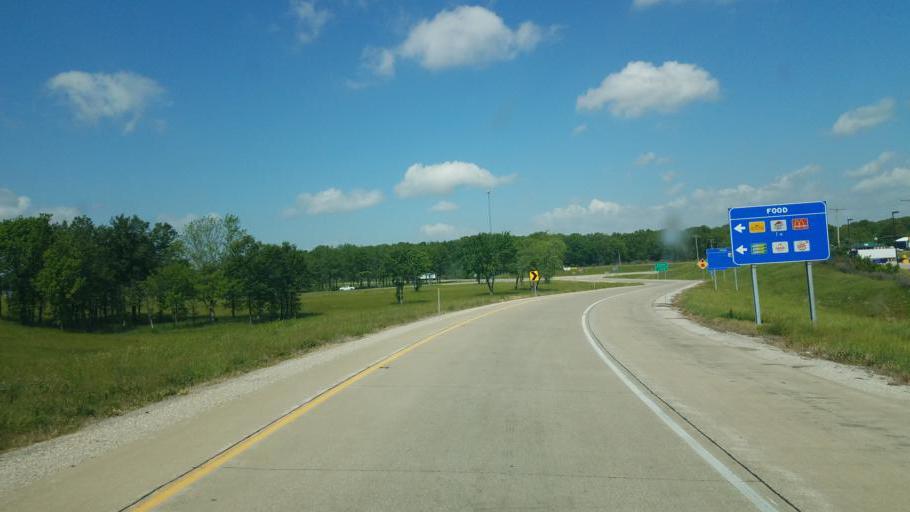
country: US
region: Illinois
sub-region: Clark County
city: Marshall
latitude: 39.4224
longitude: -87.6901
